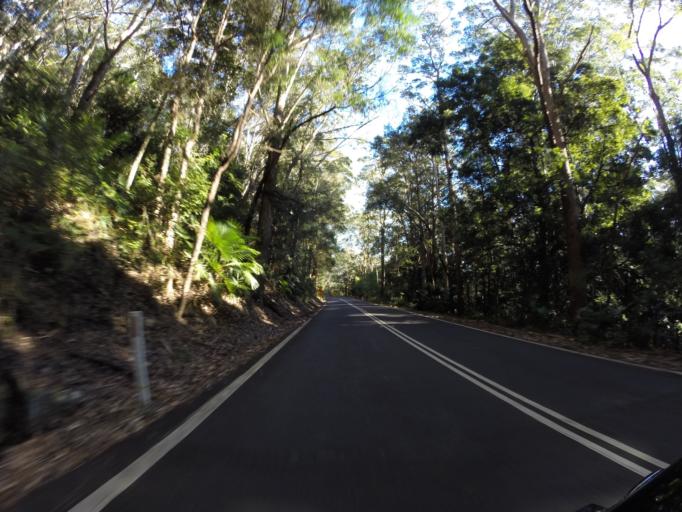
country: AU
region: New South Wales
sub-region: Wollongong
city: Helensburgh
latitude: -34.1982
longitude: 151.0108
